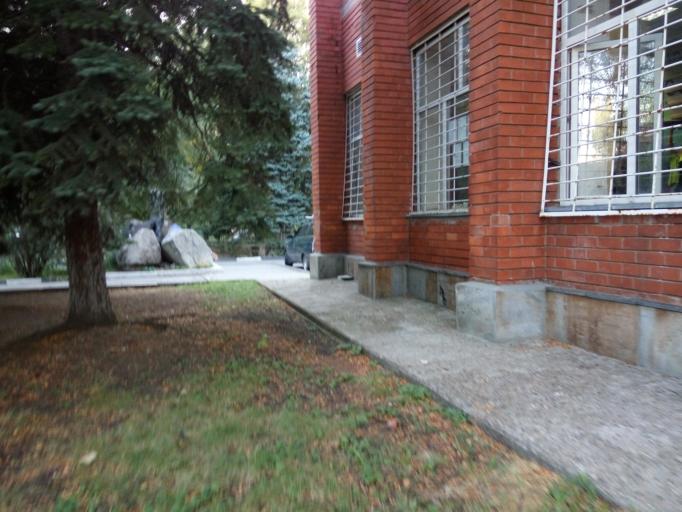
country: RU
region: Rostov
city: Imeni Chkalova
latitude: 47.2456
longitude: 39.7577
